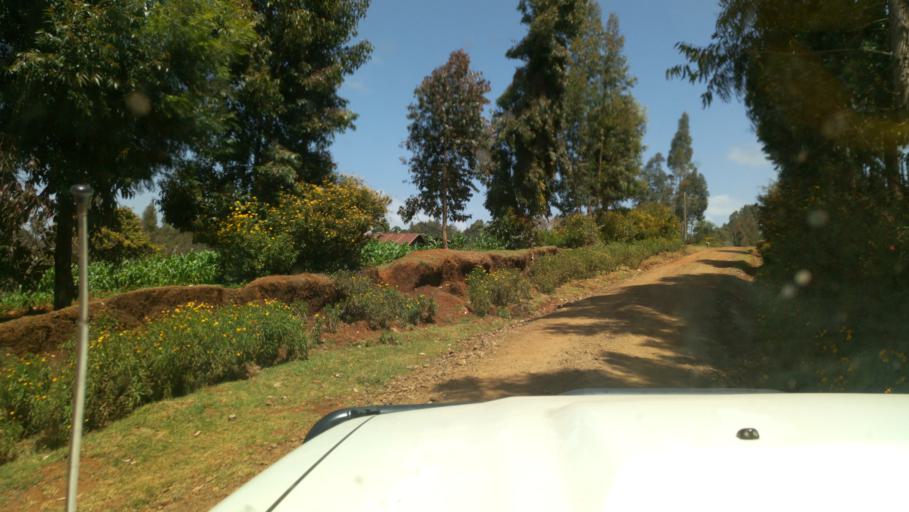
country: KE
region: Nyeri
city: Nyeri
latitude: -0.3192
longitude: 36.7792
